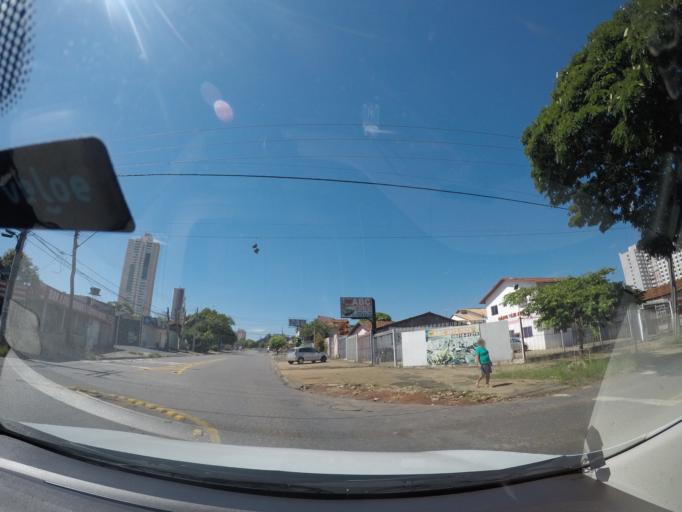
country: BR
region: Goias
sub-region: Goiania
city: Goiania
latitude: -16.7057
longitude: -49.2804
